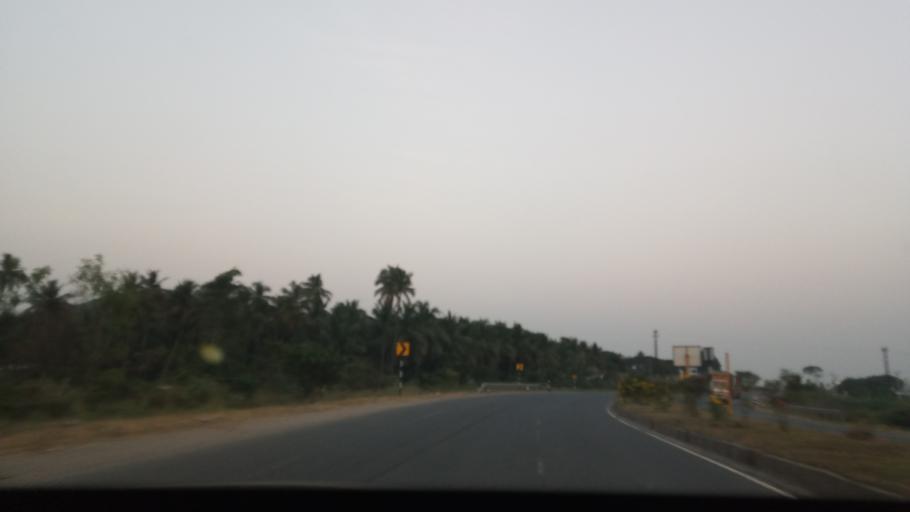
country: IN
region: Tamil Nadu
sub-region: Salem
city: Belur
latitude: 11.6522
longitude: 78.3527
